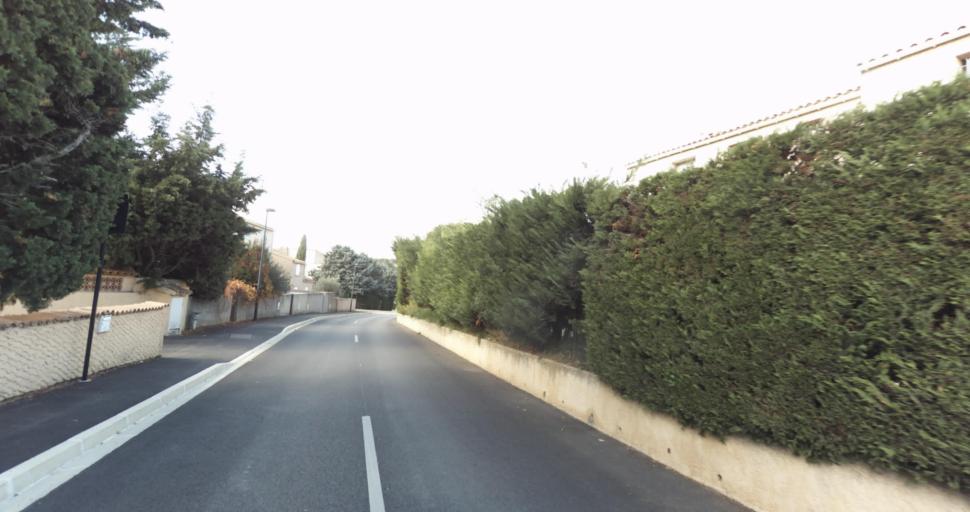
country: FR
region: Provence-Alpes-Cote d'Azur
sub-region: Departement des Bouches-du-Rhone
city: Venelles
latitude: 43.6002
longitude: 5.4892
